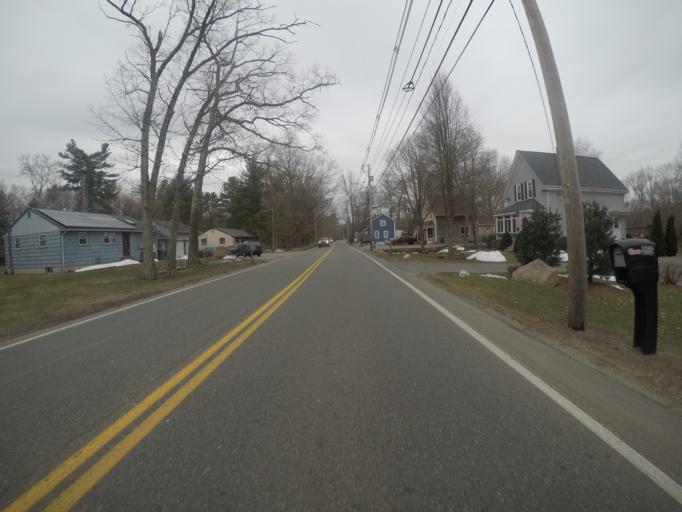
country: US
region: Massachusetts
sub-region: Bristol County
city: Easton
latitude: 42.0398
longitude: -71.0911
